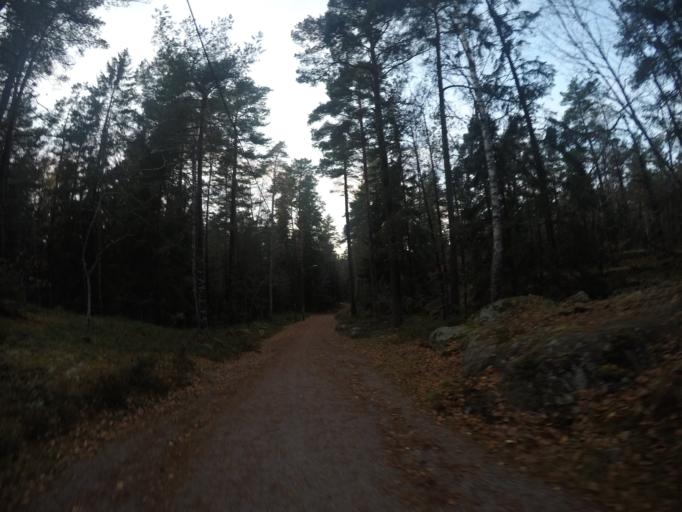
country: SE
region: Soedermanland
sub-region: Eskilstuna Kommun
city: Eskilstuna
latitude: 59.3453
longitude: 16.5181
